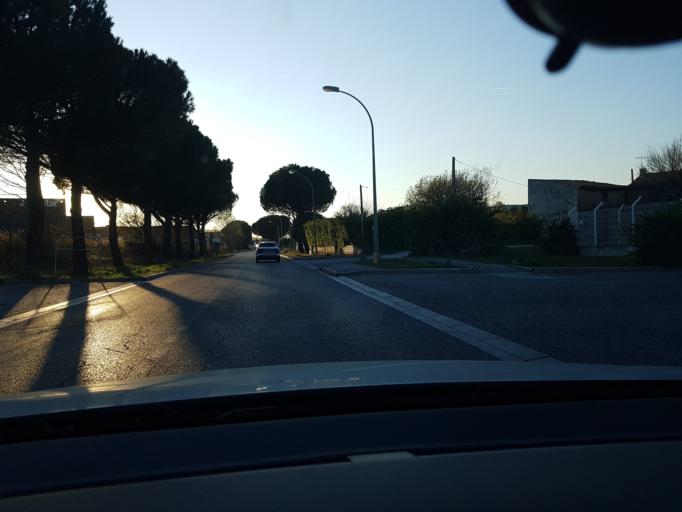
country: FR
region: Provence-Alpes-Cote d'Azur
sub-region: Departement des Bouches-du-Rhone
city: Rousset
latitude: 43.4701
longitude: 5.6032
